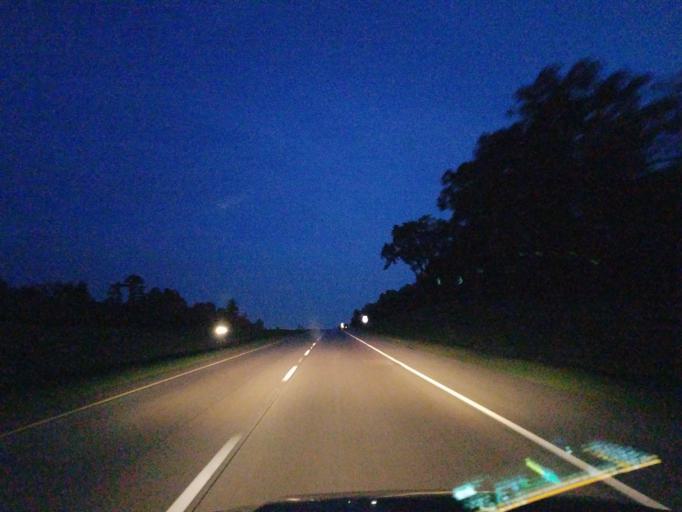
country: US
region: Mississippi
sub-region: Forrest County
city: Rawls Springs
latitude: 31.4629
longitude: -89.3227
